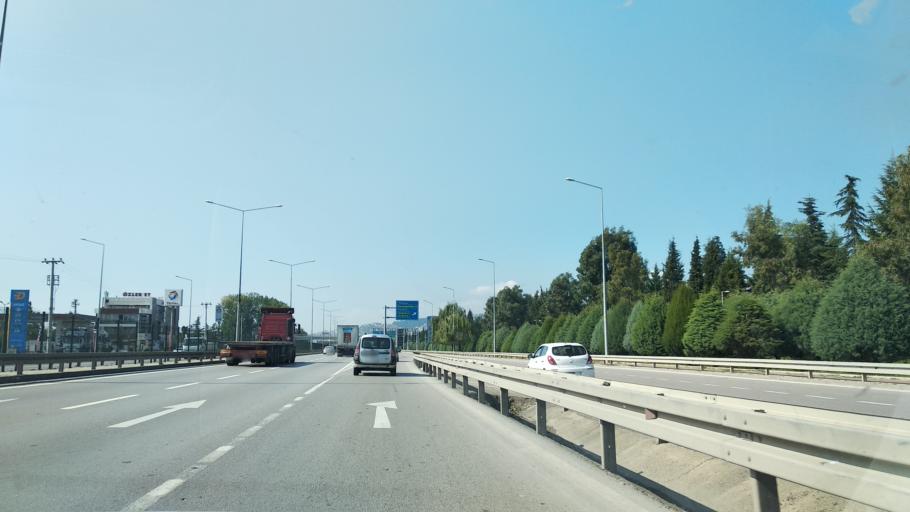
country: TR
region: Kocaeli
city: Kullar
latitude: 40.7606
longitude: 29.9745
